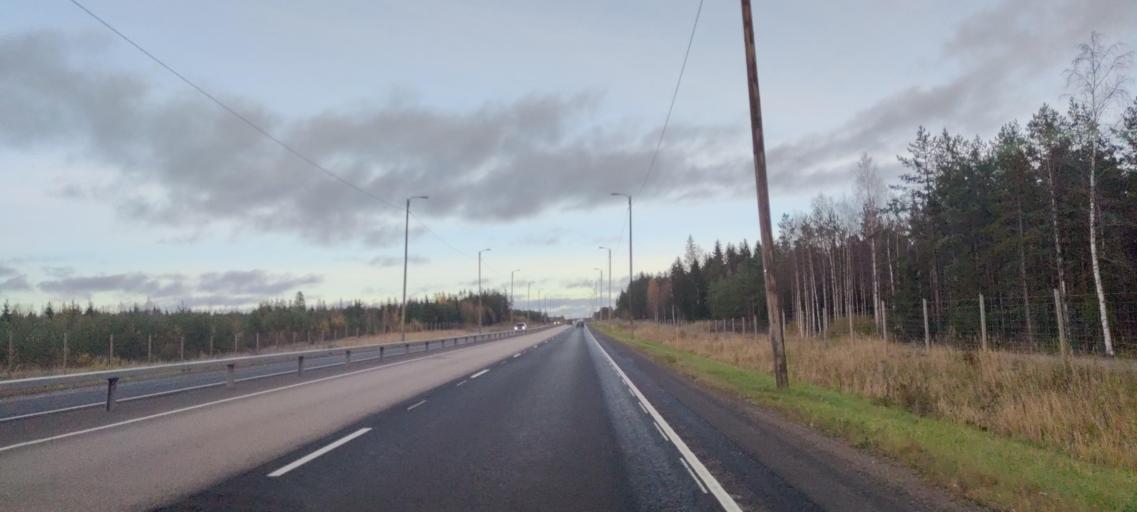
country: FI
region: Satakunta
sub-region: Pori
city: Luvia
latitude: 61.3899
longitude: 21.6824
